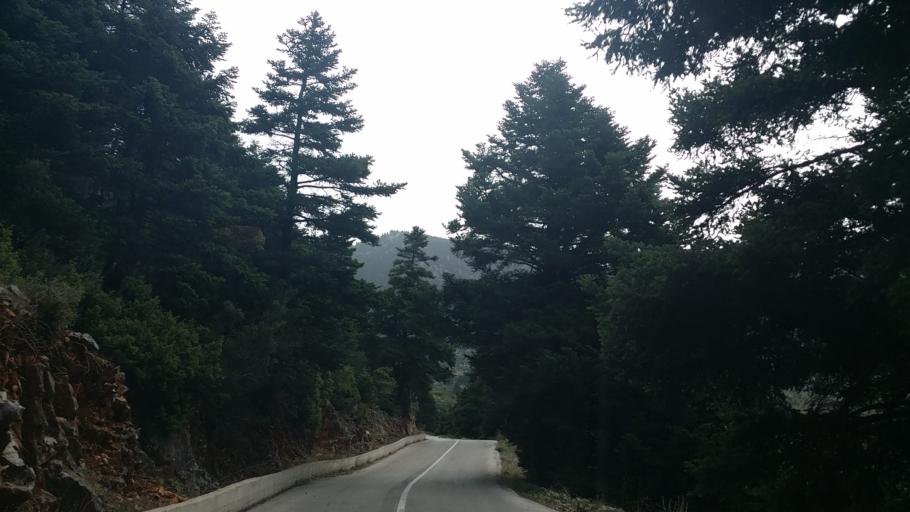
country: GR
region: Central Greece
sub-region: Nomos Voiotias
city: Livadeia
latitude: 38.3800
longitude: 22.8412
